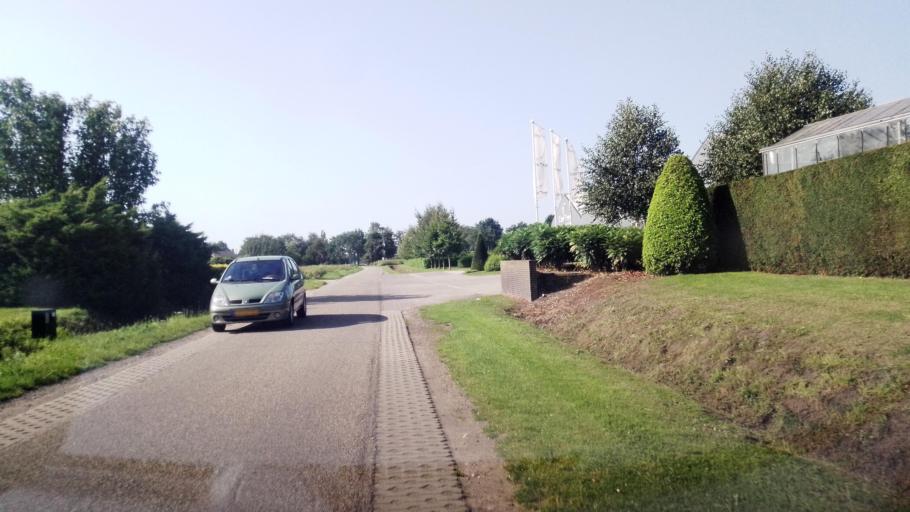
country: NL
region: Limburg
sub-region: Gemeente Venlo
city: Arcen
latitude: 51.4579
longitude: 6.1000
